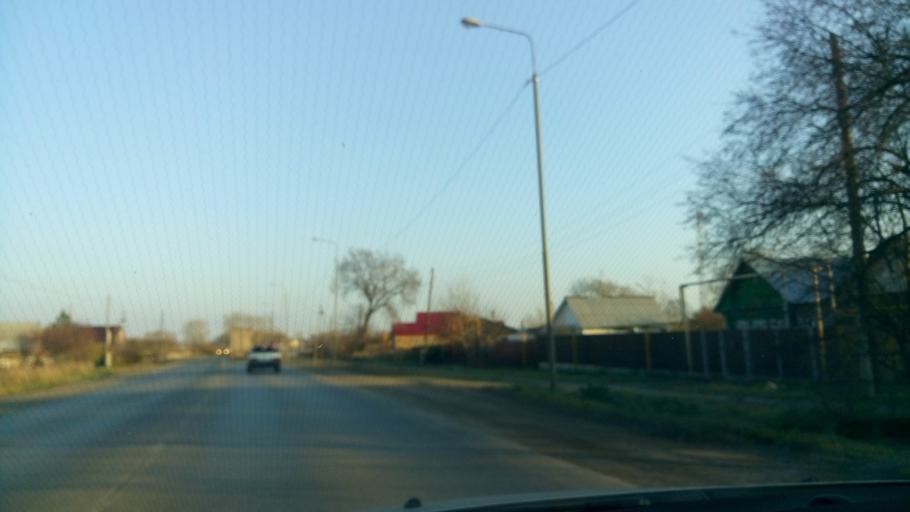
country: RU
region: Sverdlovsk
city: Bogdanovich
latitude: 56.7578
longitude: 62.0814
